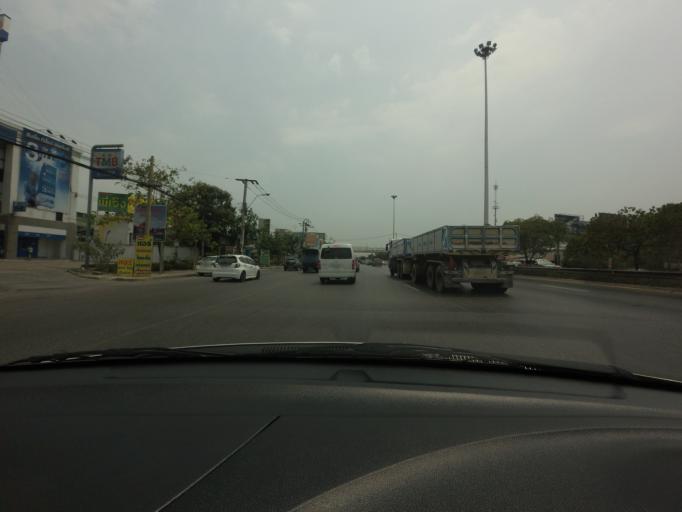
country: TH
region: Bangkok
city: Thawi Watthana
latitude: 13.7880
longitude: 100.3329
